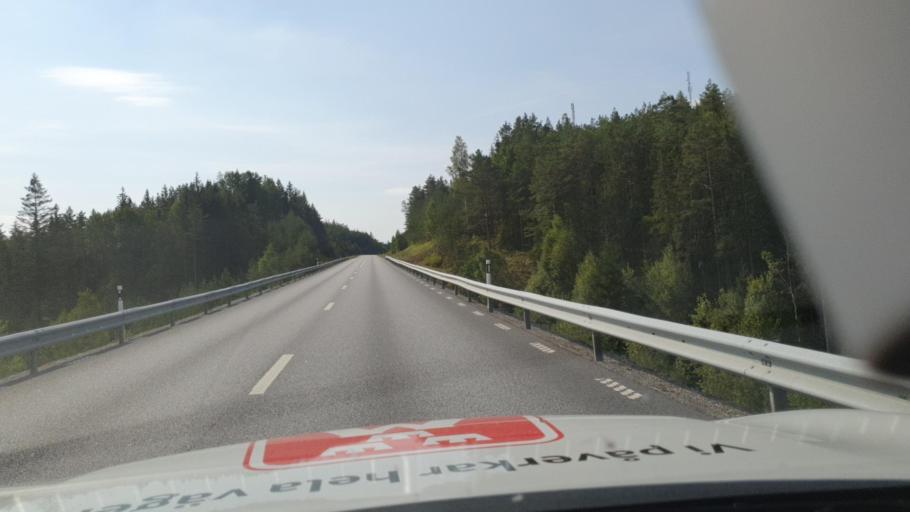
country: SE
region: Vaestra Goetaland
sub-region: Tanums Kommun
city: Tanumshede
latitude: 58.8101
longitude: 11.5992
